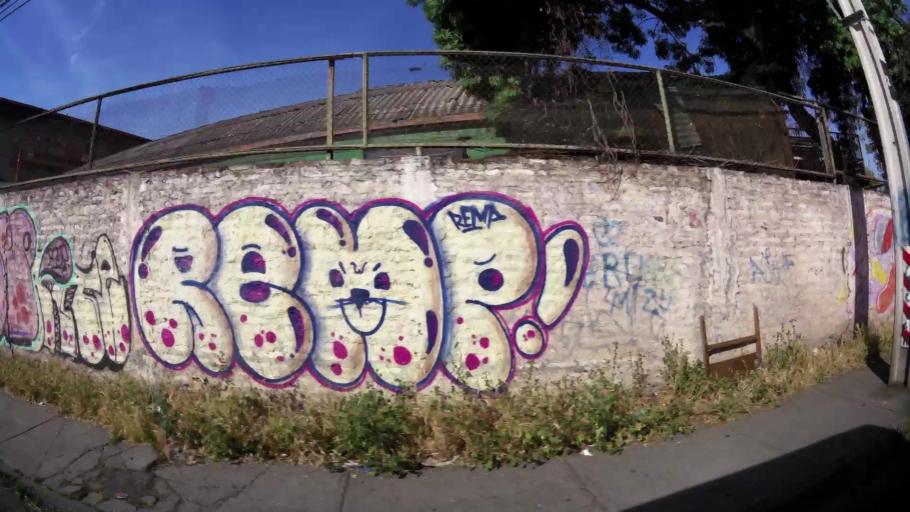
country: CL
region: Santiago Metropolitan
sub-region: Provincia de Santiago
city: Santiago
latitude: -33.5078
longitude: -70.6360
